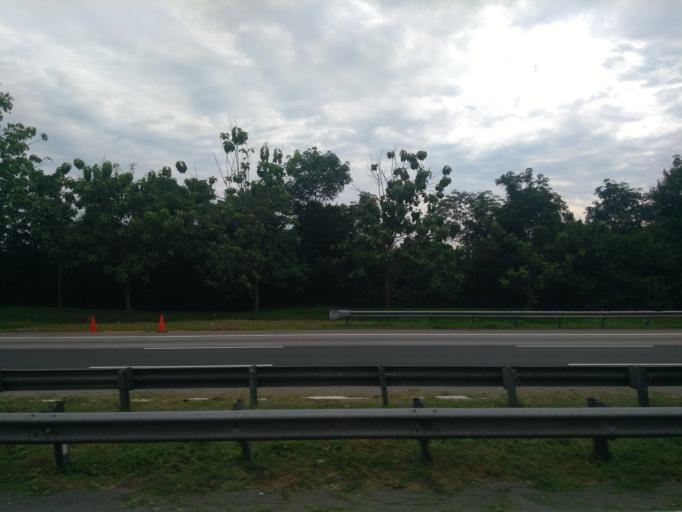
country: MY
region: Melaka
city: Pulau Sebang
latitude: 2.4325
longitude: 102.2058
